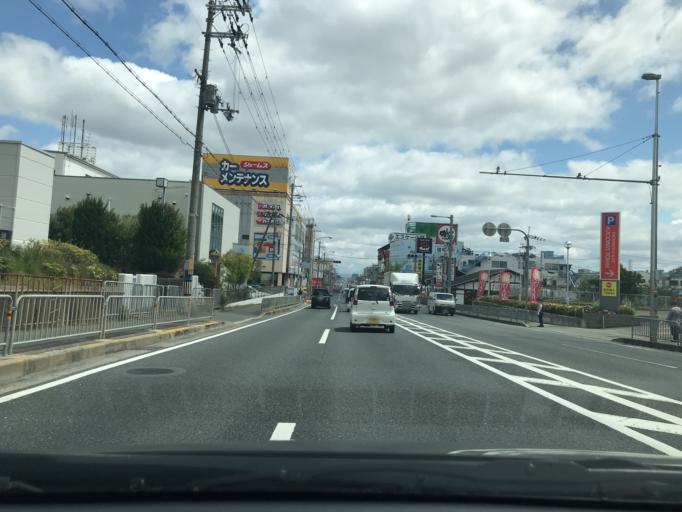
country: JP
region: Osaka
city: Ibaraki
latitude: 34.8363
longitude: 135.5303
